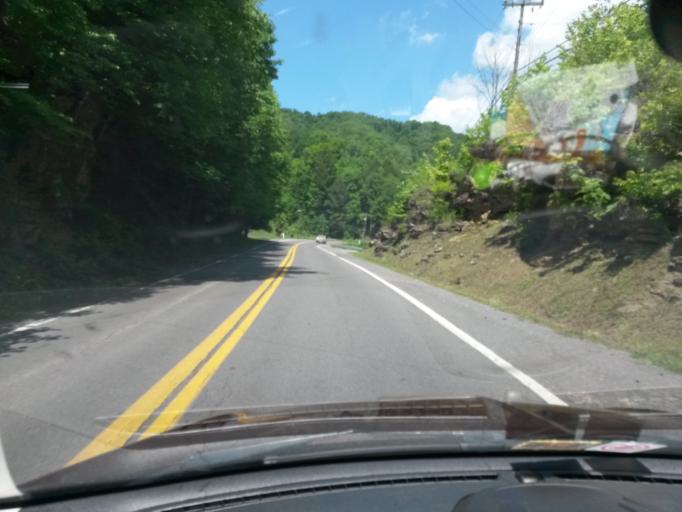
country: US
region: West Virginia
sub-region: Wyoming County
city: Pineville
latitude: 37.5029
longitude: -81.5386
